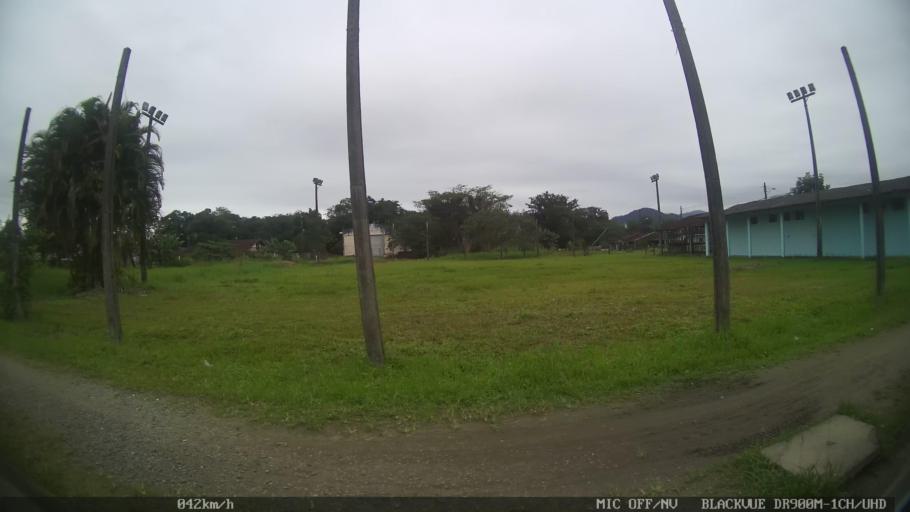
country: BR
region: Santa Catarina
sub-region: Joinville
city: Joinville
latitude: -26.2836
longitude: -48.8989
